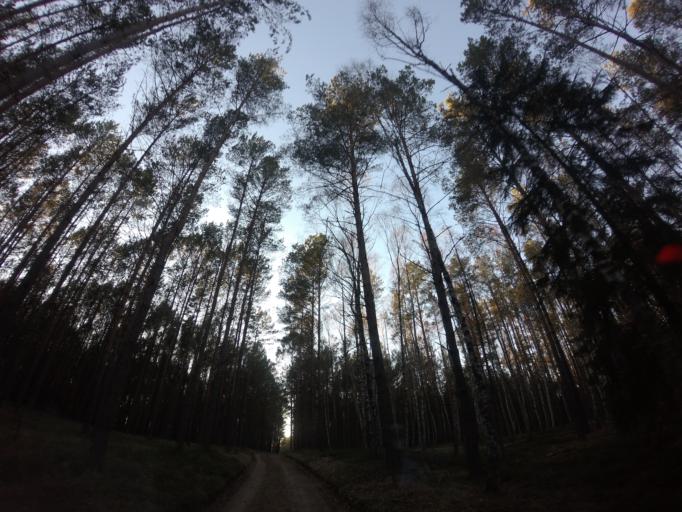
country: PL
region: West Pomeranian Voivodeship
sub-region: Powiat choszczenski
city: Drawno
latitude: 53.1131
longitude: 15.7815
